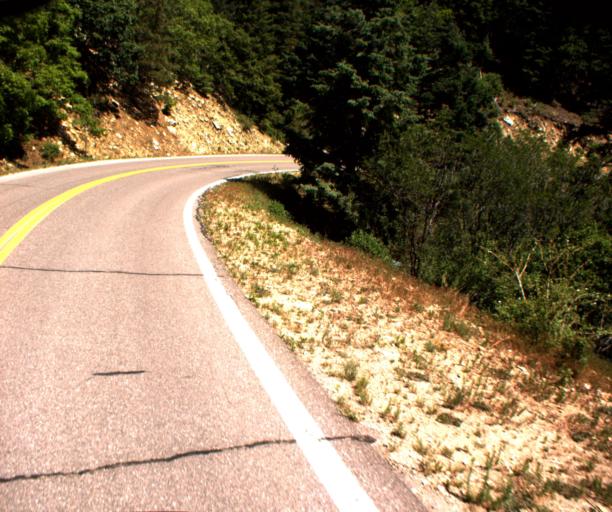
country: US
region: Arizona
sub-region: Graham County
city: Swift Trail Junction
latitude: 32.6349
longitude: -109.8419
